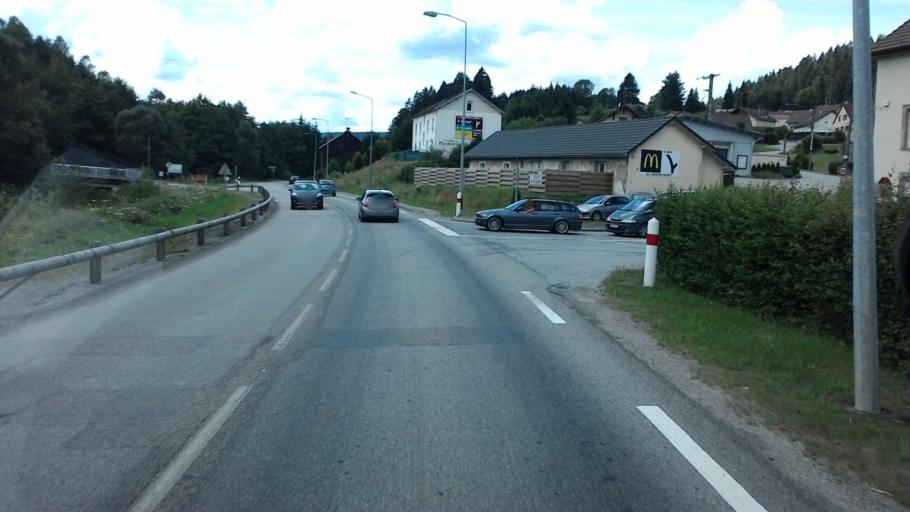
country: FR
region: Lorraine
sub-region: Departement des Vosges
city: Le Tholy
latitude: 48.0852
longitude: 6.7643
